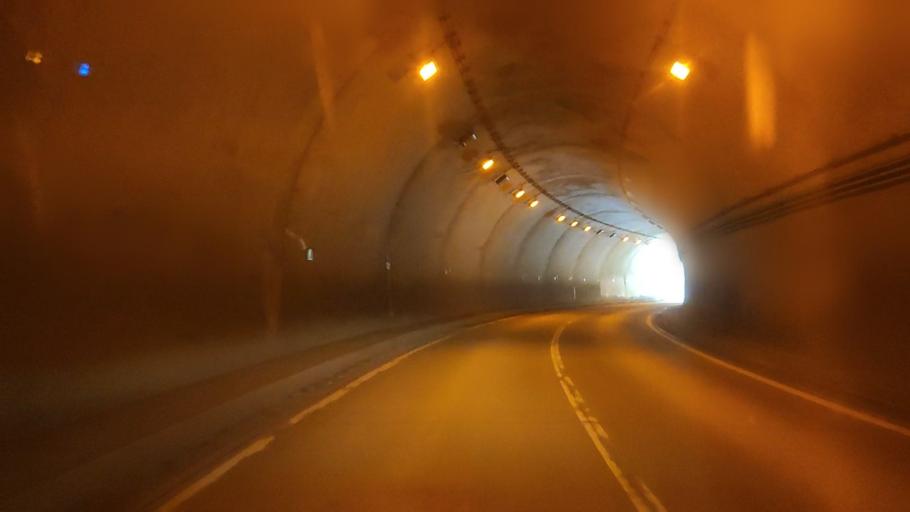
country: JP
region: Kumamoto
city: Hitoyoshi
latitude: 32.4137
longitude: 130.8436
